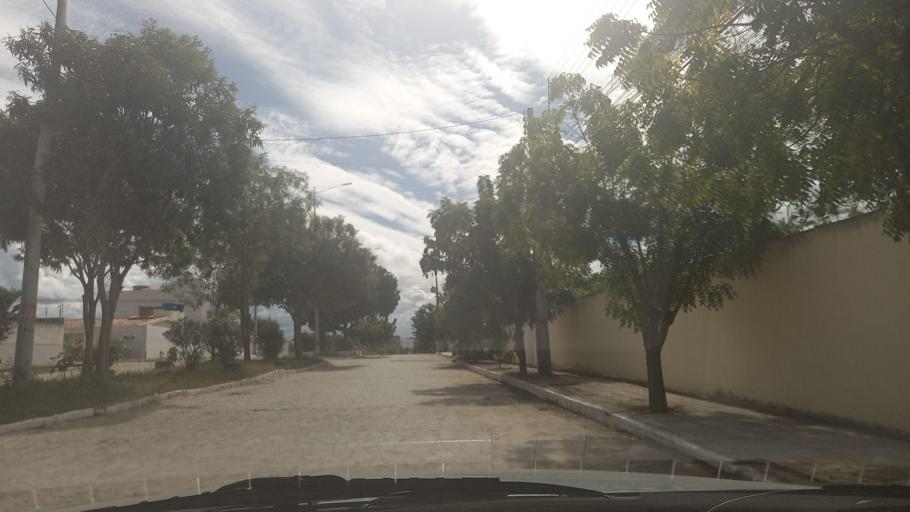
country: BR
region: Pernambuco
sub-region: Caruaru
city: Caruaru
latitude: -8.2919
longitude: -35.9894
